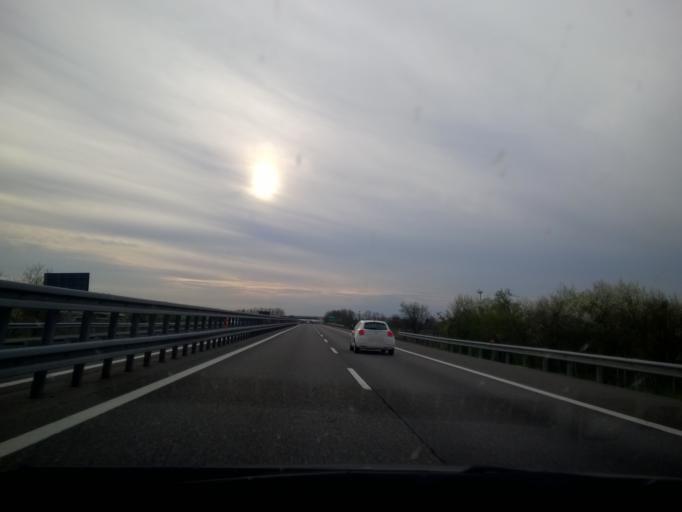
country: IT
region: Lombardy
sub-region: Provincia di Pavia
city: Stradella
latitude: 45.0832
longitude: 9.3096
